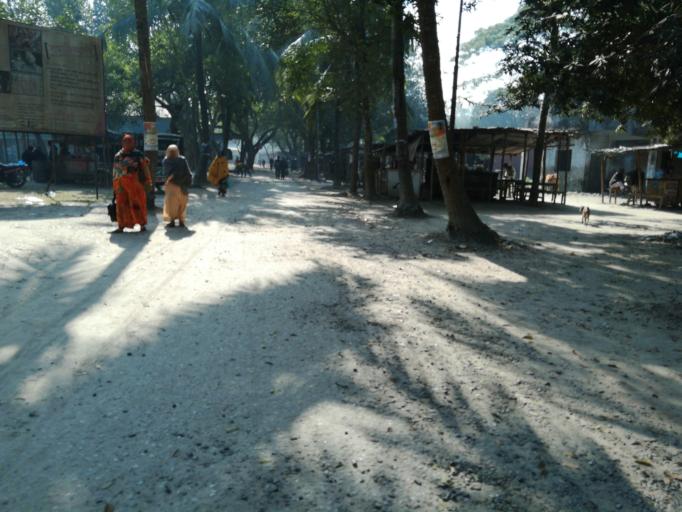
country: BD
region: Rangpur Division
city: Rangpur
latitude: 25.5698
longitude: 89.2733
